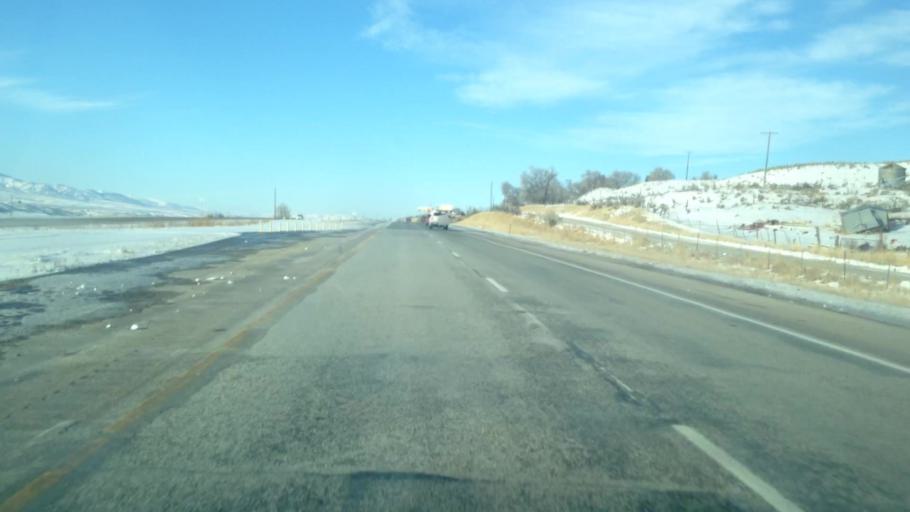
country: US
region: Idaho
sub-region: Oneida County
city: Malad City
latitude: 42.5514
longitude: -112.1741
